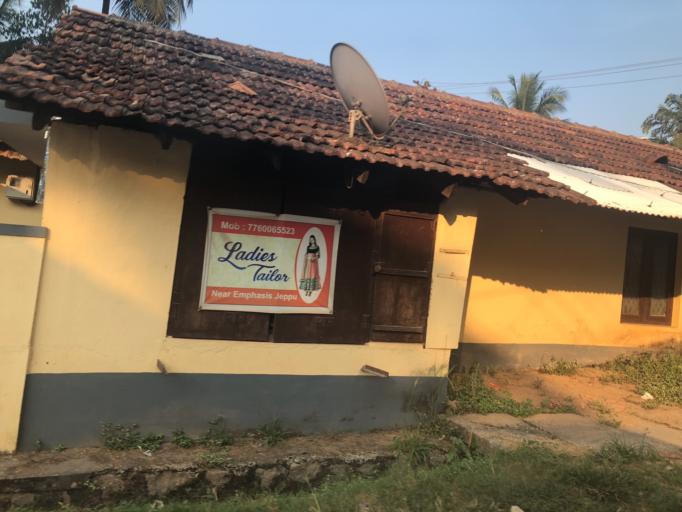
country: IN
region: Karnataka
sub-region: Dakshina Kannada
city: Ullal
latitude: 12.8458
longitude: 74.8506
